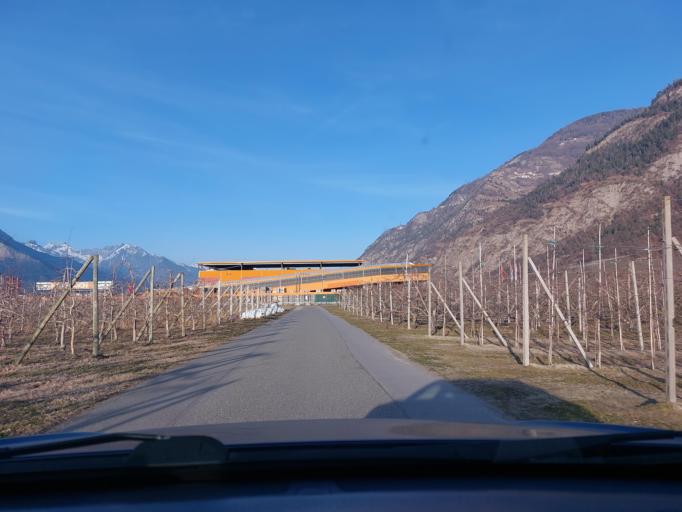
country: CH
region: Valais
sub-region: Martigny District
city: Riddes
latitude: 46.1639
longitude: 7.2075
